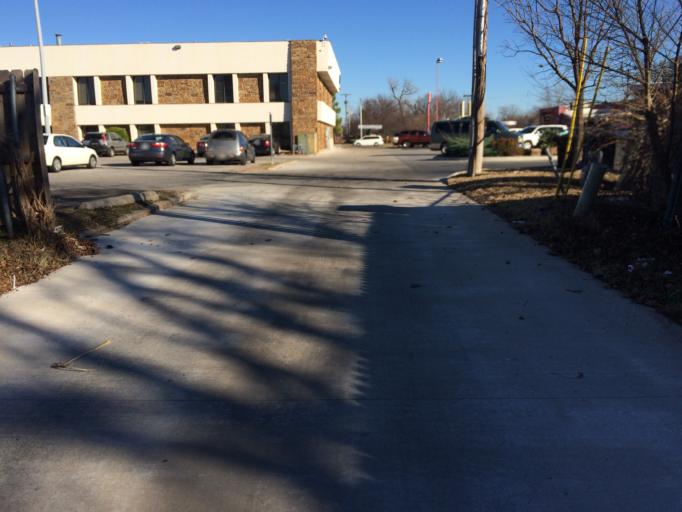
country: US
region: Oklahoma
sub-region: Cleveland County
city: Norman
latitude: 35.2282
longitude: -97.4422
